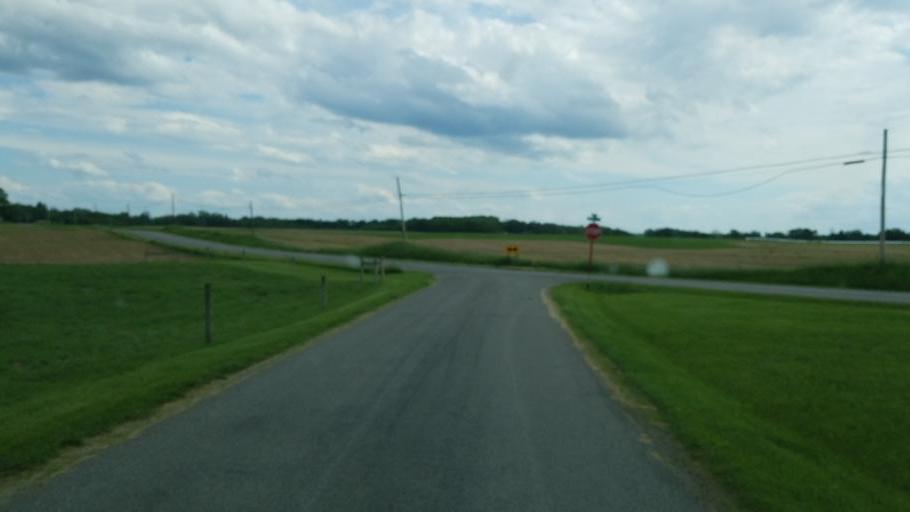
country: US
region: Ohio
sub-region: Richland County
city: Shelby
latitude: 40.9162
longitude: -82.5707
